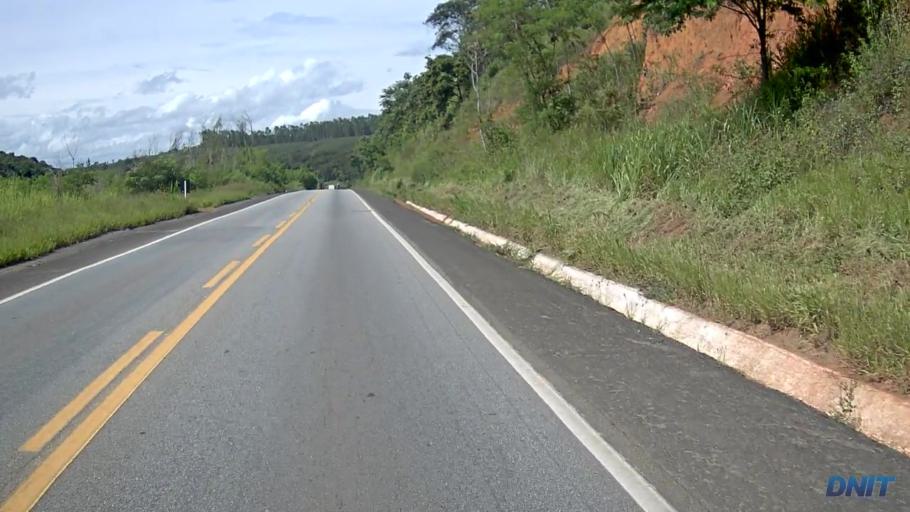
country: BR
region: Minas Gerais
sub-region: Ipaba
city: Ipaba
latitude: -19.4083
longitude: -42.4872
